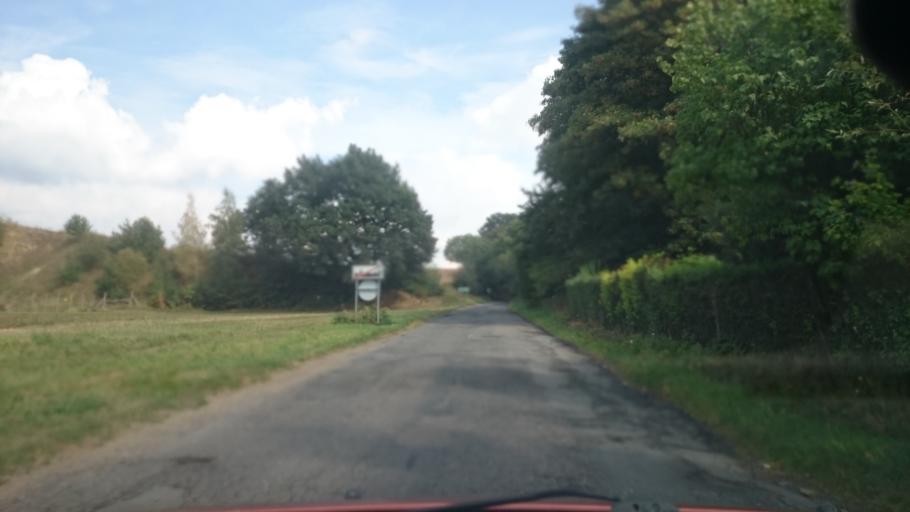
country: PL
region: Lower Silesian Voivodeship
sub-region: Powiat zabkowicki
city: Ziebice
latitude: 50.5501
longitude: 17.0543
